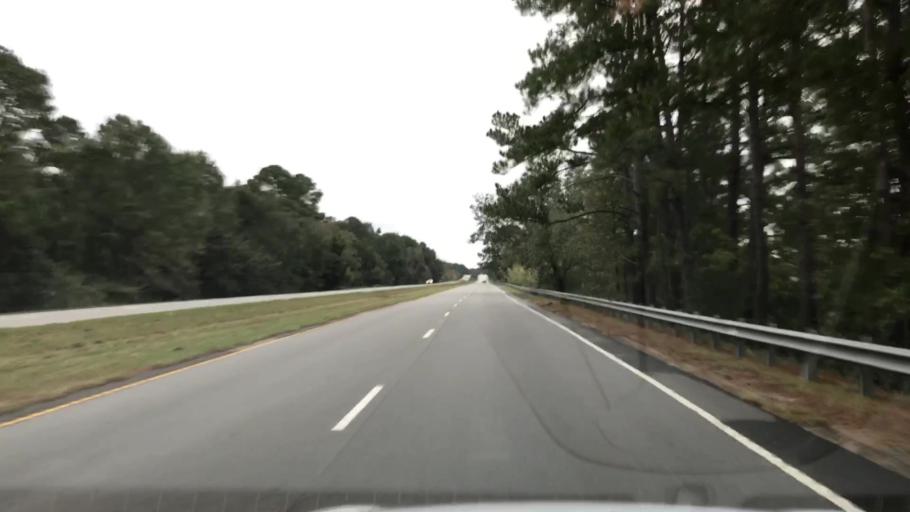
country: US
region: South Carolina
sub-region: Georgetown County
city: Georgetown
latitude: 33.2009
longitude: -79.3911
